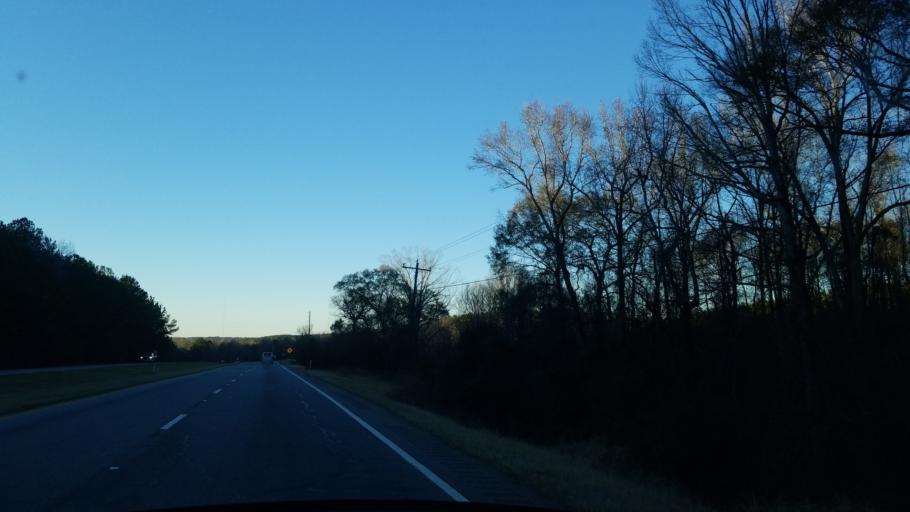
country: US
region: Georgia
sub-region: Chattahoochee County
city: Cusseta
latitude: 32.2562
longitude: -84.7243
